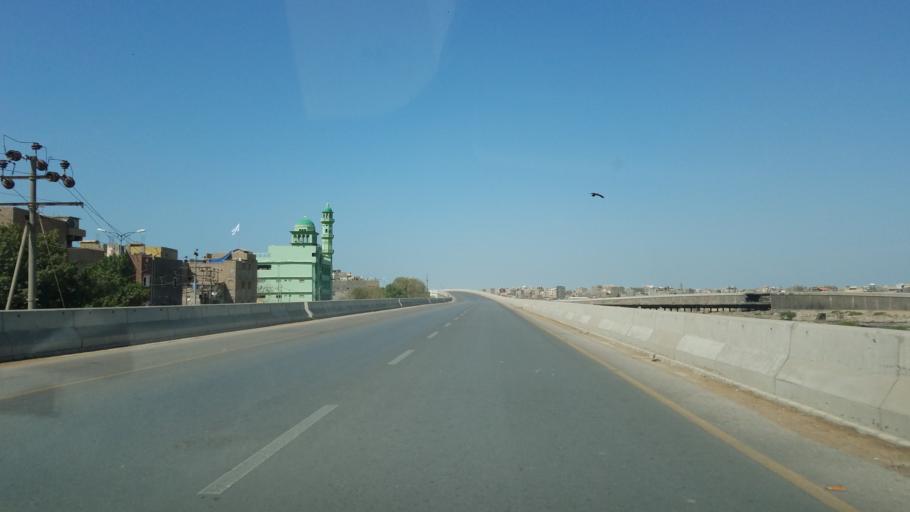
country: PK
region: Sindh
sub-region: Karachi District
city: Karachi
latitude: 24.8803
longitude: 66.9991
